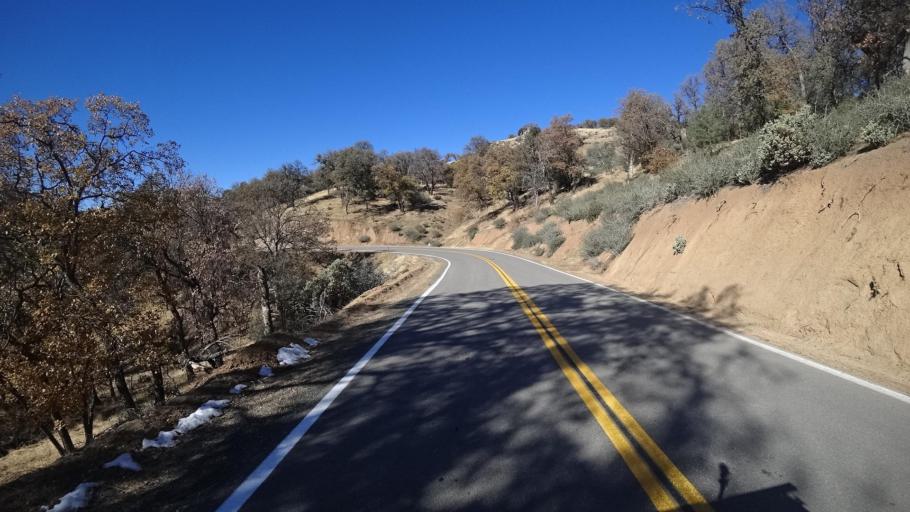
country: US
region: California
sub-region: Kern County
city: Alta Sierra
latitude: 35.7426
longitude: -118.6042
